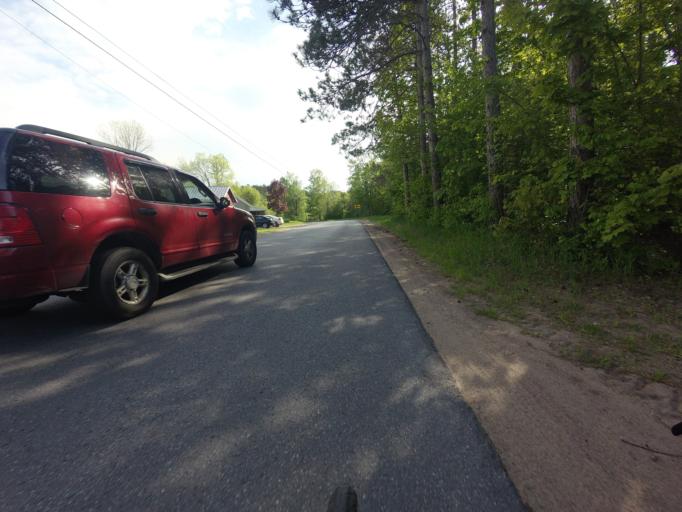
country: US
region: New York
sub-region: St. Lawrence County
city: Gouverneur
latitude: 44.1866
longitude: -75.2811
